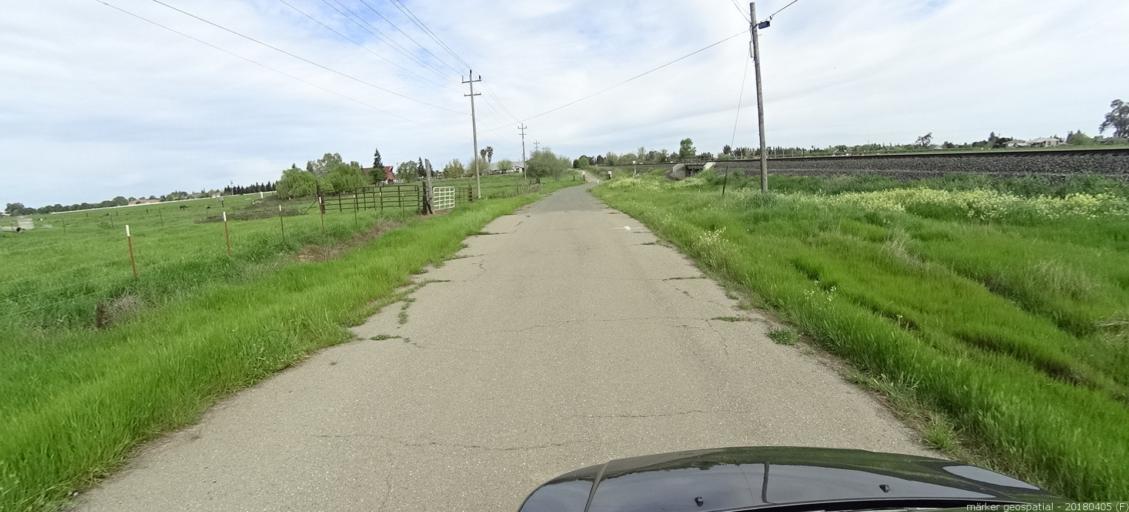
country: US
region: California
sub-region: Sacramento County
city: Galt
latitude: 38.2760
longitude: -121.3155
